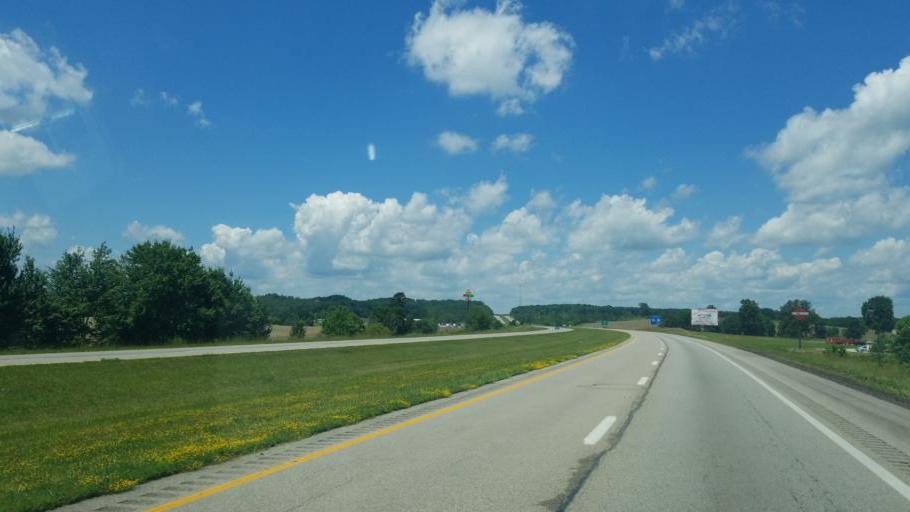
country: US
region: Ohio
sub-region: Gallia County
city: Gallipolis
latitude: 38.8745
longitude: -82.2861
